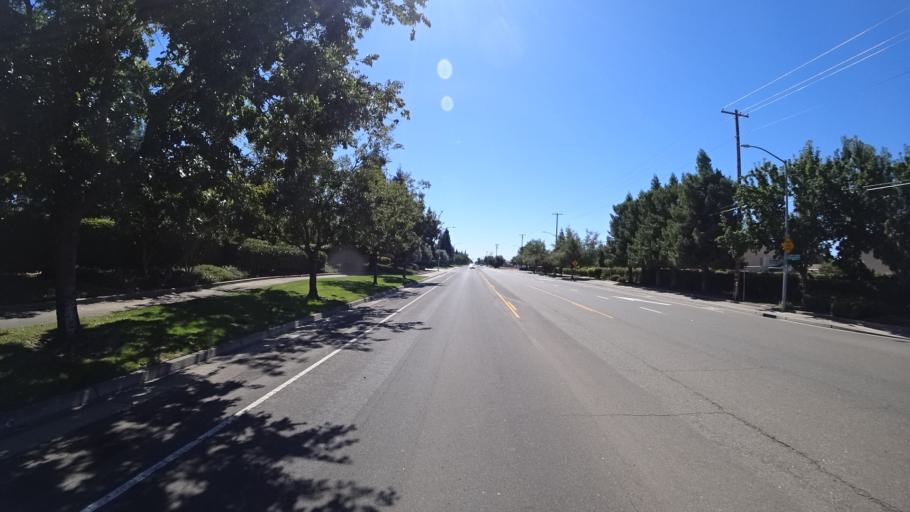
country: US
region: California
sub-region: Sacramento County
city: Elk Grove
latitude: 38.4213
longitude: -121.3345
